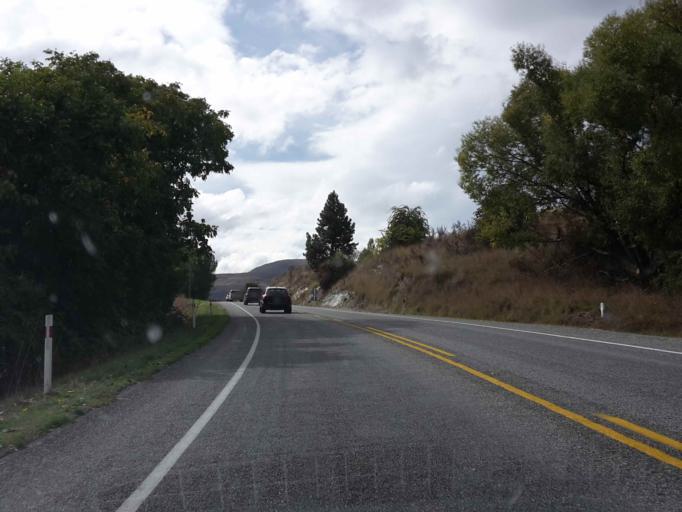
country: NZ
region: Otago
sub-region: Queenstown-Lakes District
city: Arrowtown
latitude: -44.9851
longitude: 168.8195
